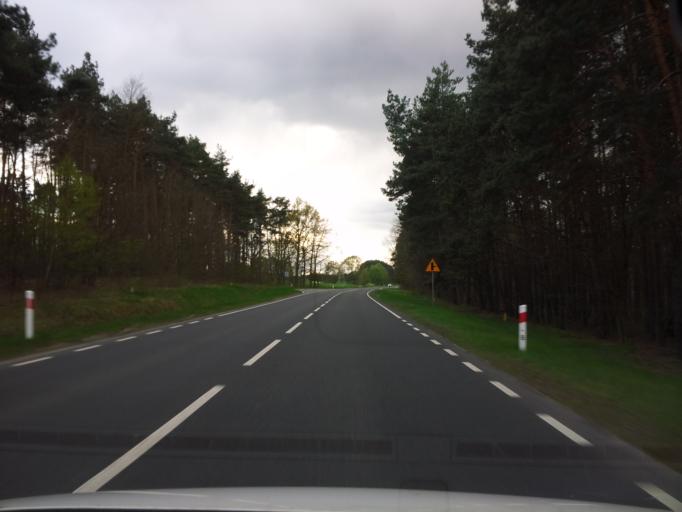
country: PL
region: Lubusz
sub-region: Powiat krosnienski
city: Krosno Odrzanskie
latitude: 52.0164
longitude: 15.0881
